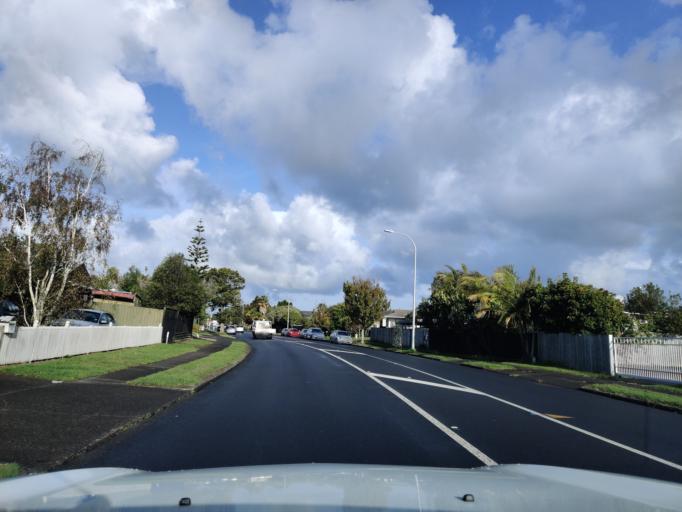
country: NZ
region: Auckland
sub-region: Auckland
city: Pakuranga
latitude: -36.9098
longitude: 174.8988
